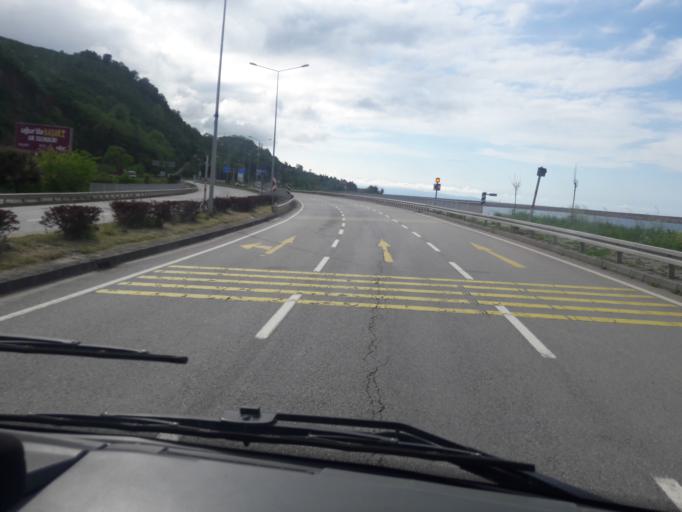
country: TR
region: Giresun
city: Piraziz
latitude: 40.9577
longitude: 38.1171
